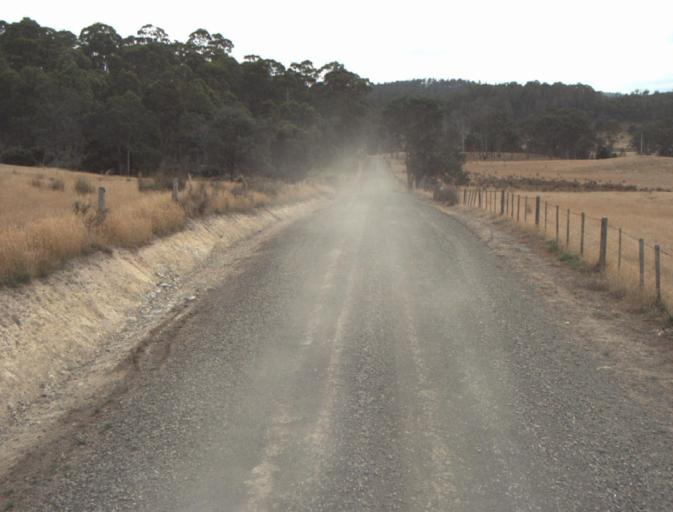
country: AU
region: Tasmania
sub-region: Northern Midlands
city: Evandale
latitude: -41.4684
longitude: 147.4473
